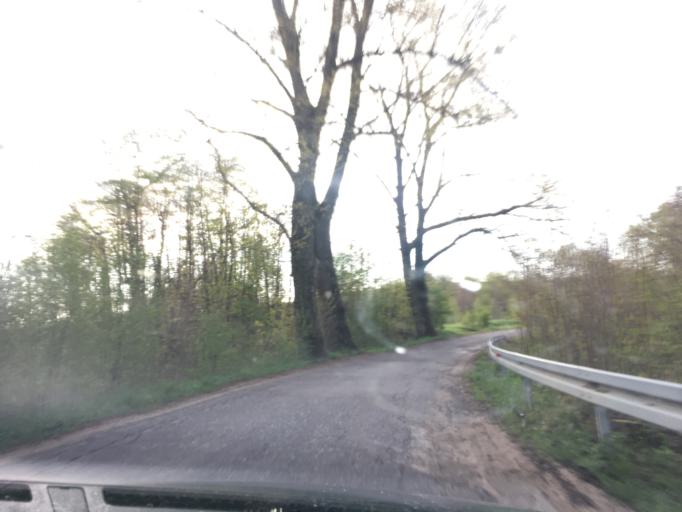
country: PL
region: Warmian-Masurian Voivodeship
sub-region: Powiat ostrodzki
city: Dabrowno
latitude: 53.4276
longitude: 20.0202
